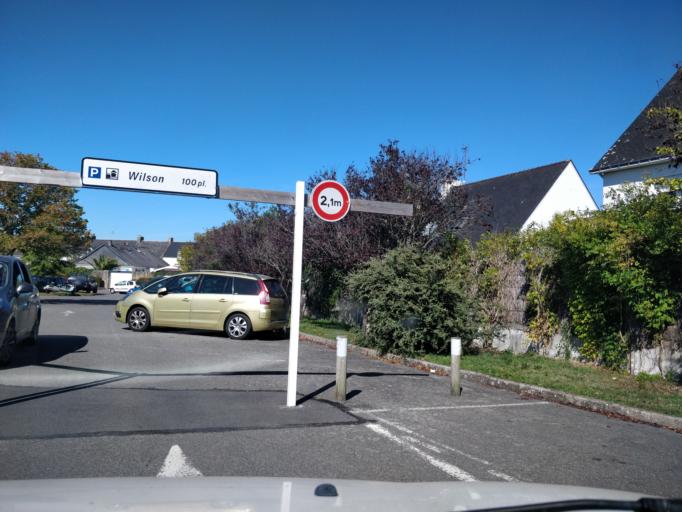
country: FR
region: Brittany
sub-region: Departement du Morbihan
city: Locmariaquer
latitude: 47.5673
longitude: -2.9430
